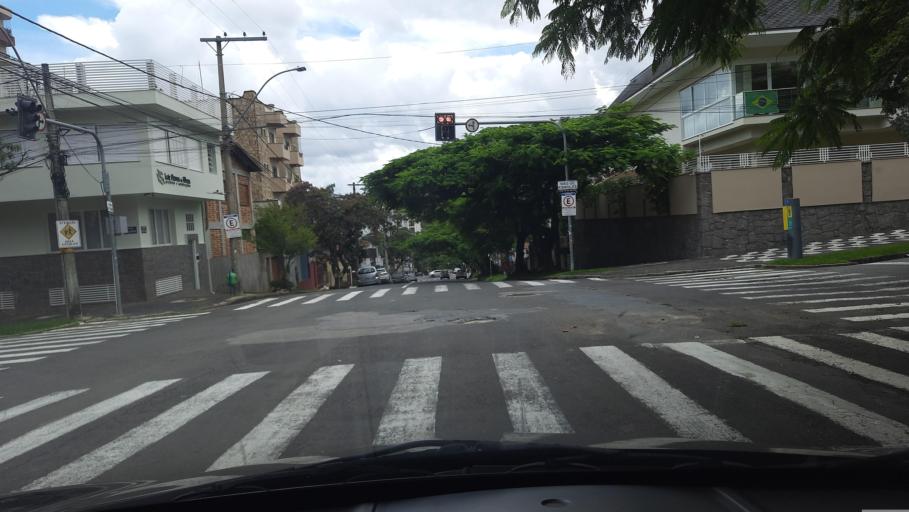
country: BR
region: Minas Gerais
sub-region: Pocos De Caldas
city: Pocos de Caldas
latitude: -21.7820
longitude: -46.5681
